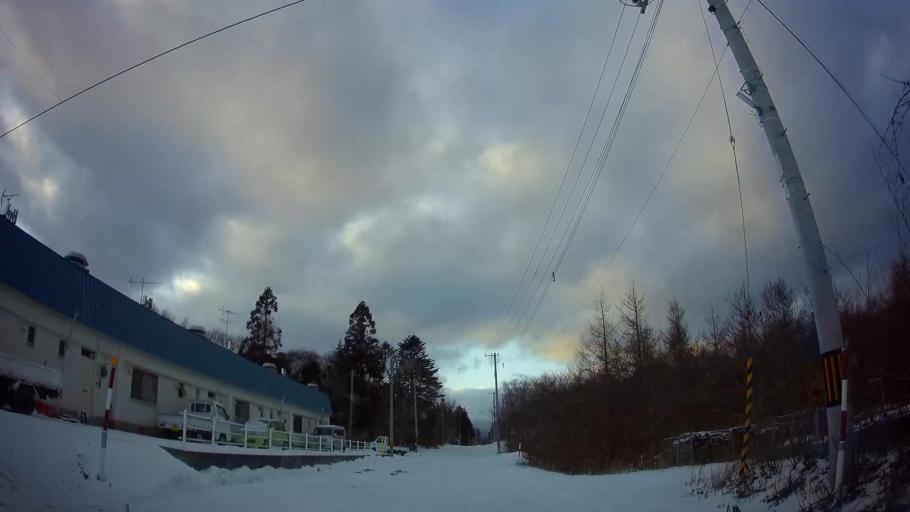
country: JP
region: Hokkaido
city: Nanae
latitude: 42.0203
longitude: 140.8397
